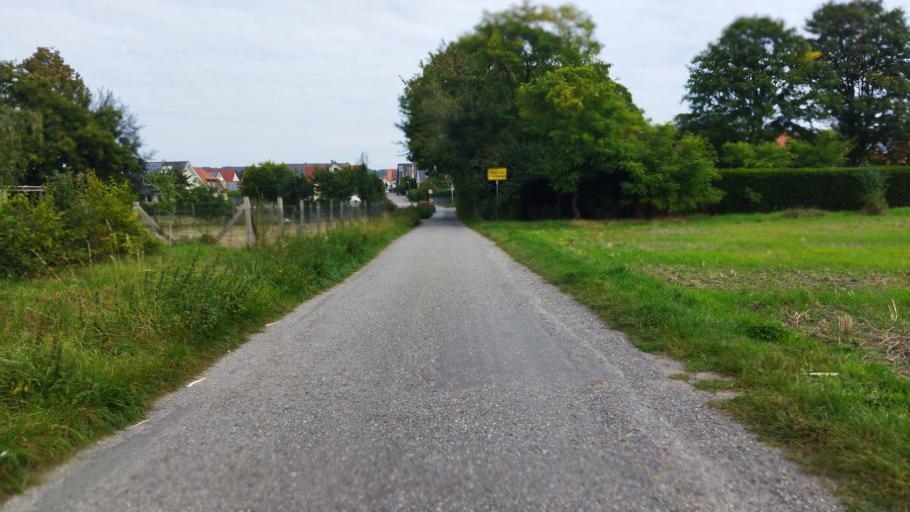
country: DE
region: Lower Saxony
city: Hilter
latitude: 52.1280
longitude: 8.1470
